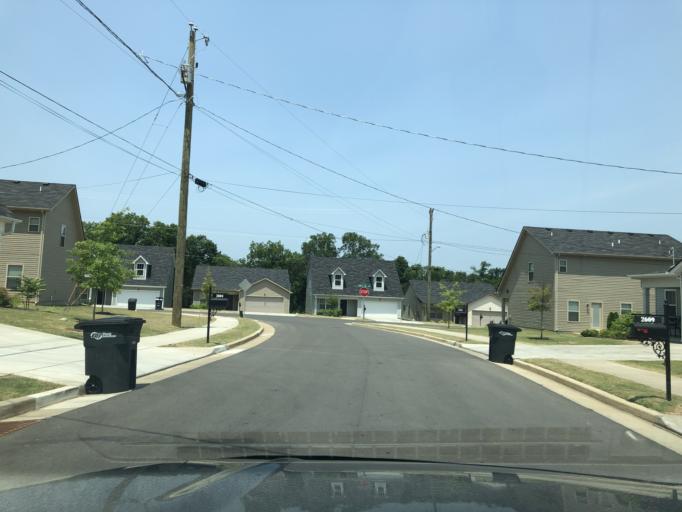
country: US
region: Tennessee
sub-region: Rutherford County
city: La Vergne
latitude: 36.0588
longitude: -86.6081
